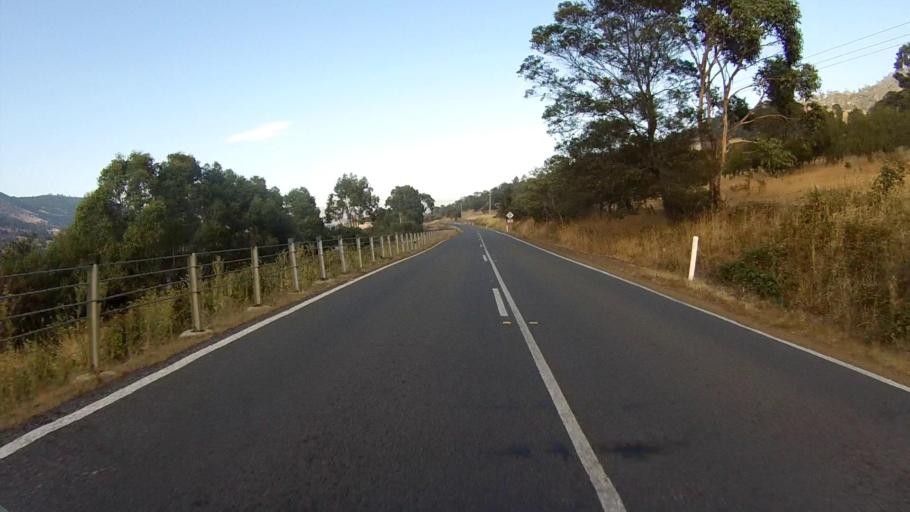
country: AU
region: Tasmania
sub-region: Glenorchy
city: Granton
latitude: -42.7506
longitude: 147.1516
